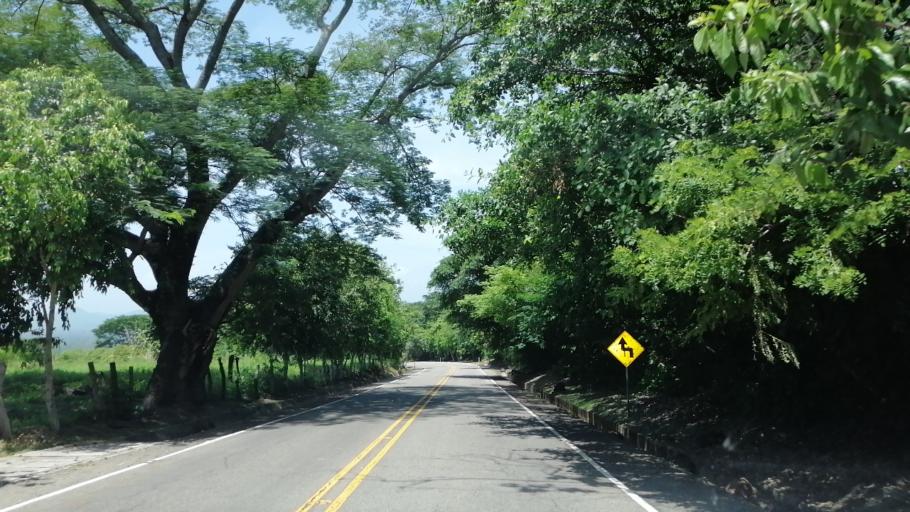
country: SV
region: Chalatenango
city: Nueva Concepcion
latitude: 14.1592
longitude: -89.3129
